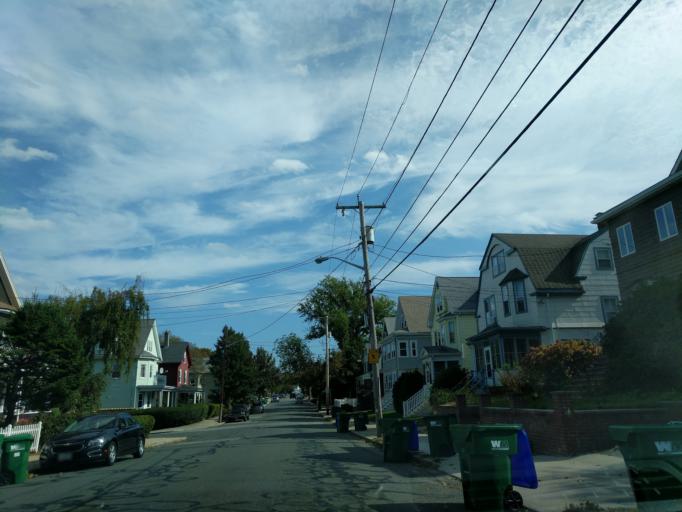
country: US
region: Massachusetts
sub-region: Middlesex County
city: Medford
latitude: 42.4136
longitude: -71.1182
